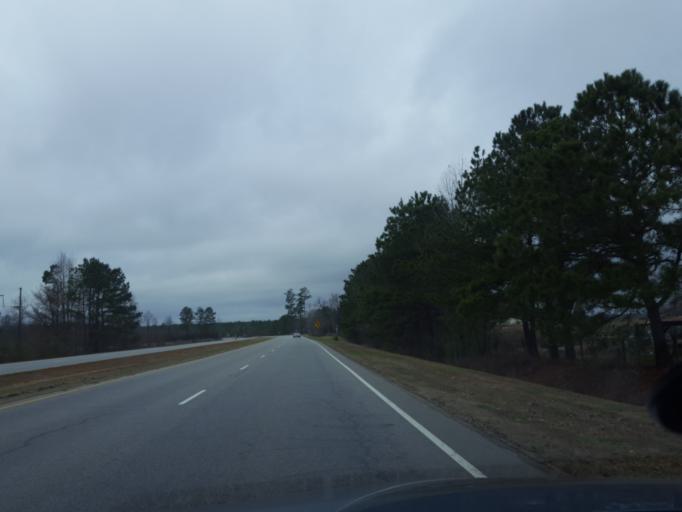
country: US
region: North Carolina
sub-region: Martin County
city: Williamston
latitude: 35.8109
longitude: -76.9104
